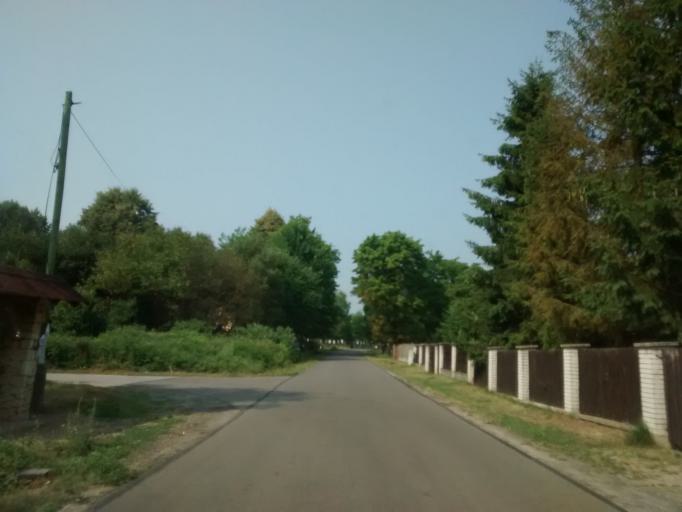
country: PL
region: Silesian Voivodeship
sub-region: Powiat zawiercianski
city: Wlodowice
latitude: 50.6110
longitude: 19.5041
